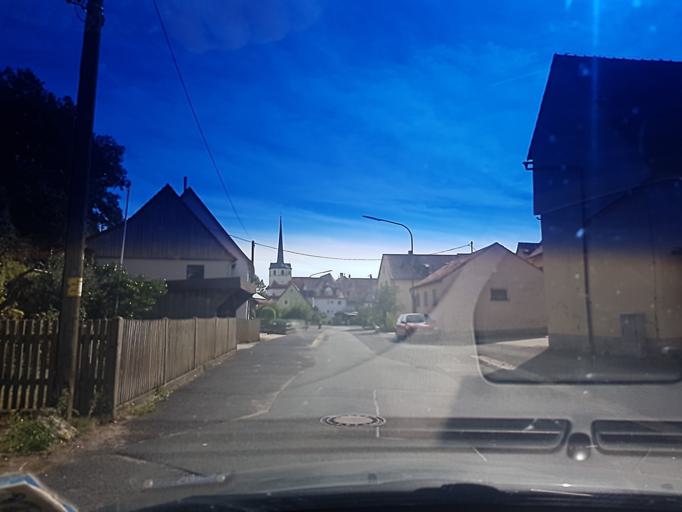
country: DE
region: Bavaria
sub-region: Regierungsbezirk Mittelfranken
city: Wachenroth
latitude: 49.7886
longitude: 10.6959
